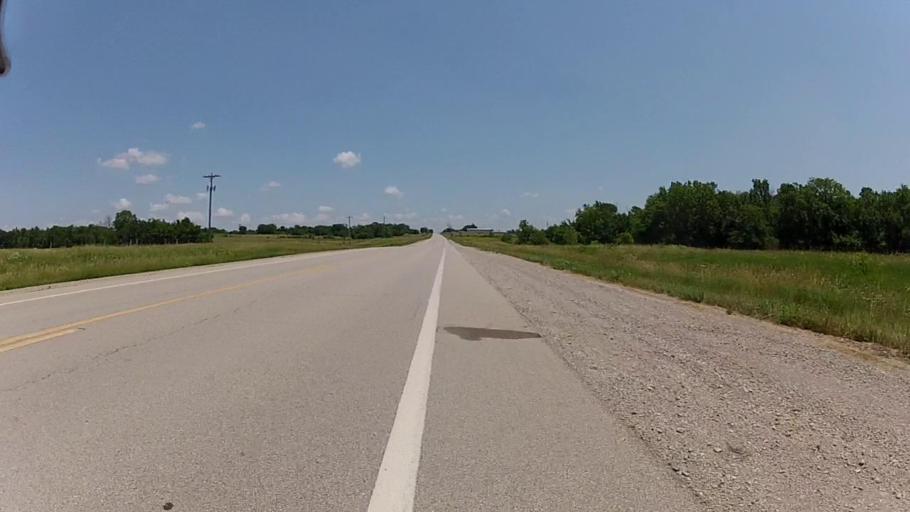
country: US
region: Kansas
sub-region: Montgomery County
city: Cherryvale
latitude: 37.1929
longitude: -95.4884
